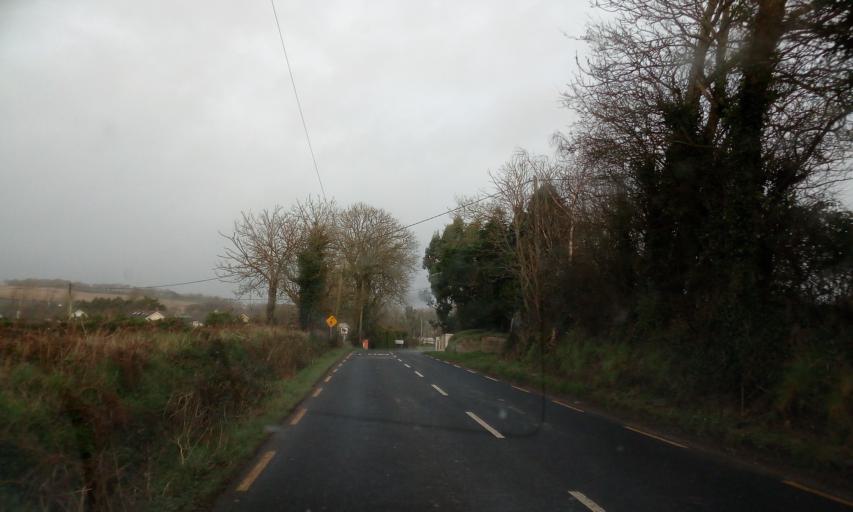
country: IE
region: Leinster
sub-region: Loch Garman
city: New Ross
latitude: 52.2635
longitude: -6.7508
